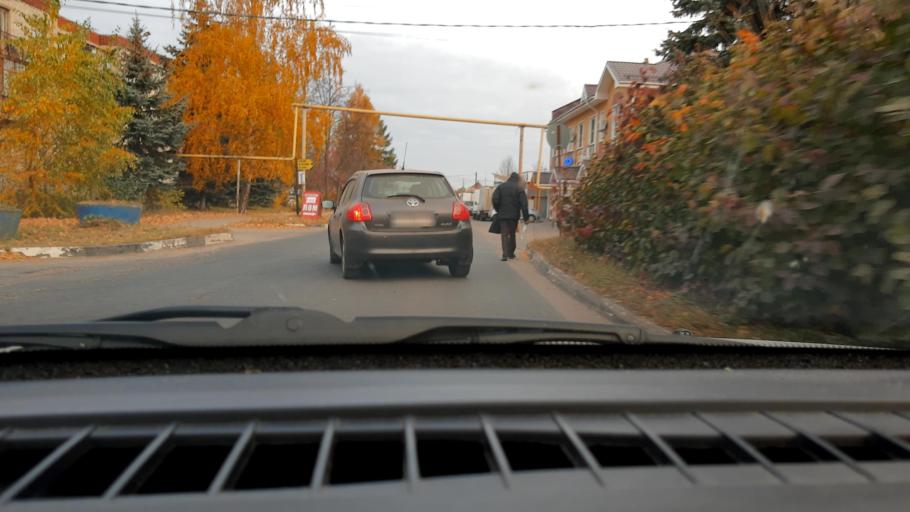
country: RU
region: Nizjnij Novgorod
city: Burevestnik
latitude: 56.2052
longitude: 43.8800
